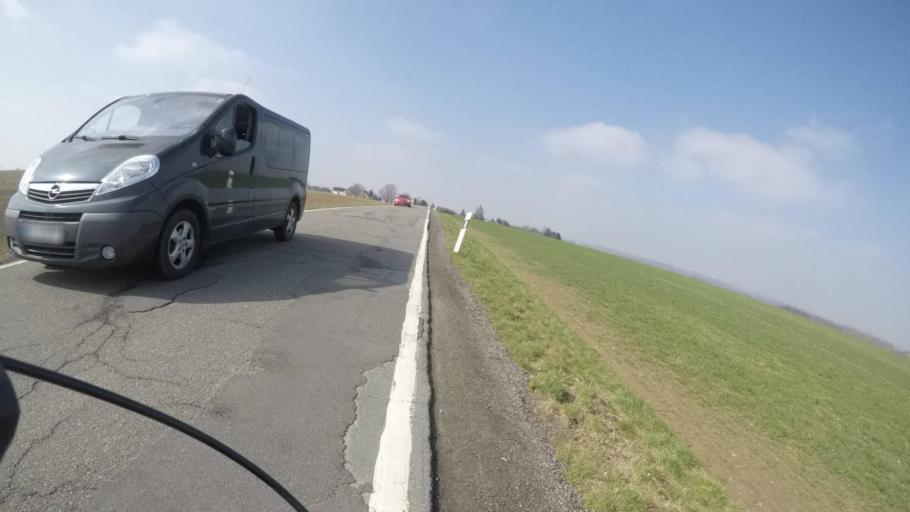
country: DE
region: Saxony
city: Niederfrohna
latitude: 50.8844
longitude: 12.7073
